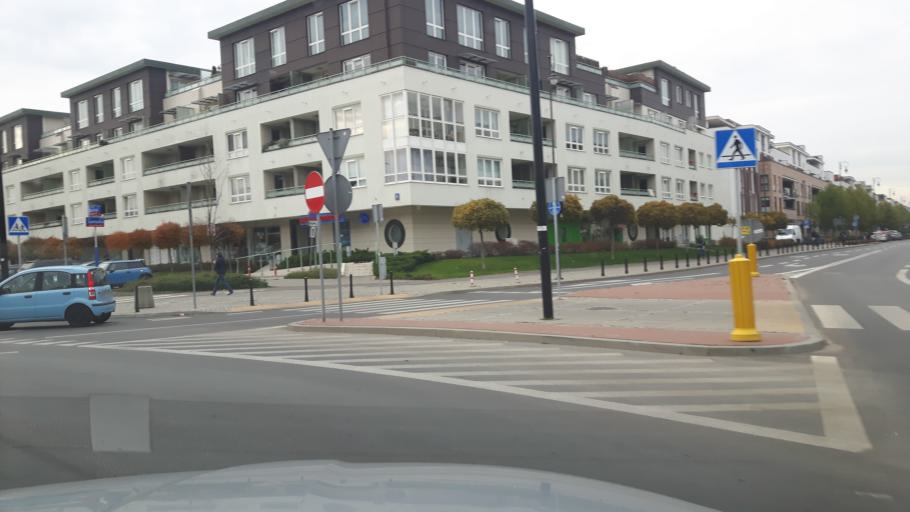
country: PL
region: Masovian Voivodeship
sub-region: Warszawa
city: Wilanow
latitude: 52.1581
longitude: 21.0809
